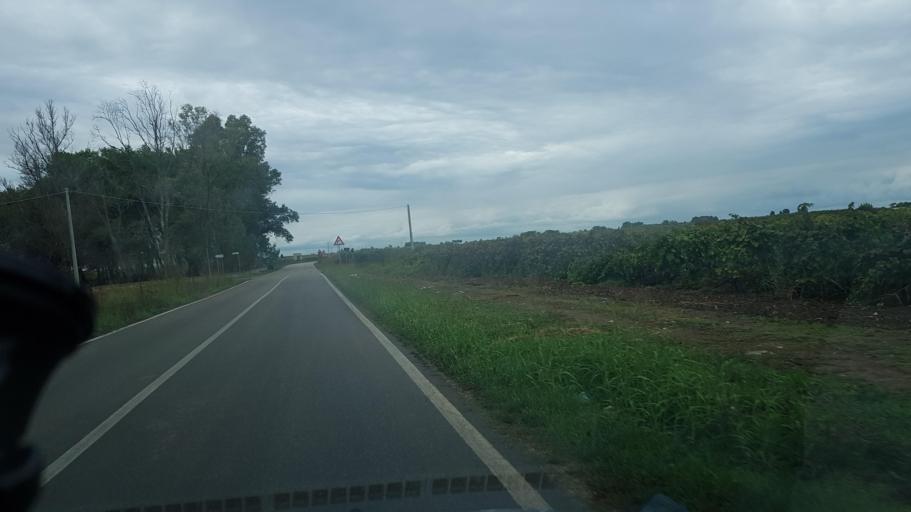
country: IT
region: Apulia
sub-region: Provincia di Lecce
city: Carmiano
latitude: 40.3558
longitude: 18.0231
